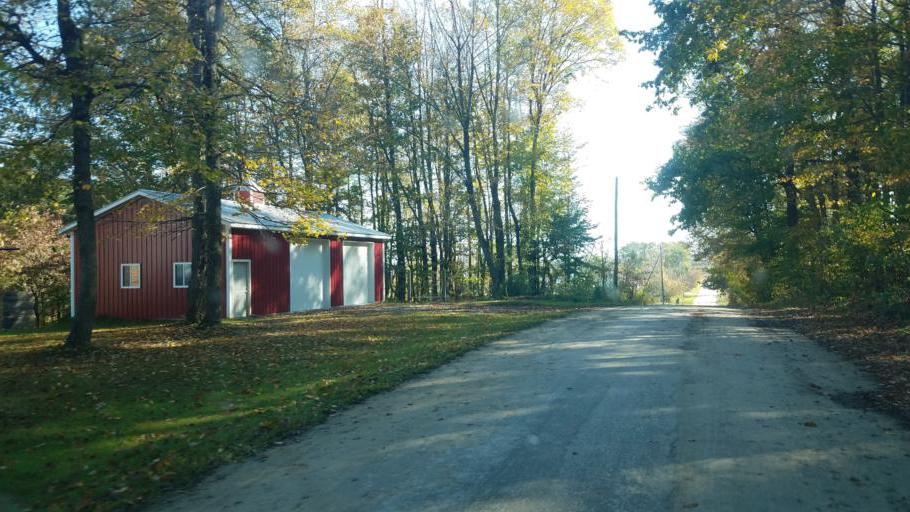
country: US
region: Ohio
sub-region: Richland County
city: Lexington
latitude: 40.6156
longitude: -82.6350
